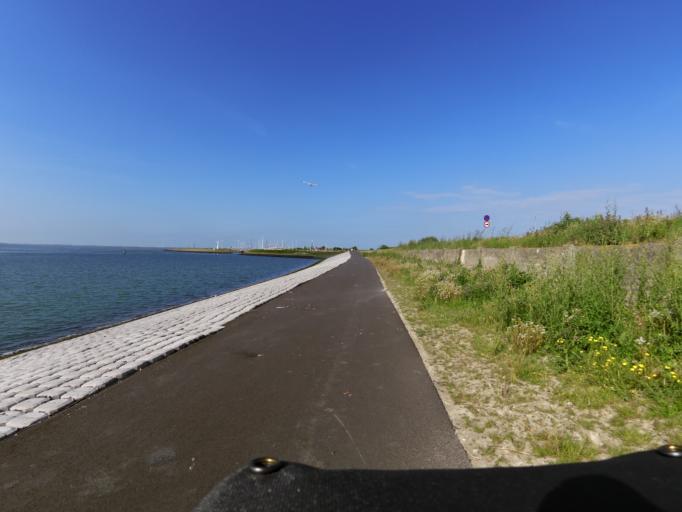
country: NL
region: Zeeland
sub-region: Schouwen-Duiveland
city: Haamstede
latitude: 51.6779
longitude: 3.7611
